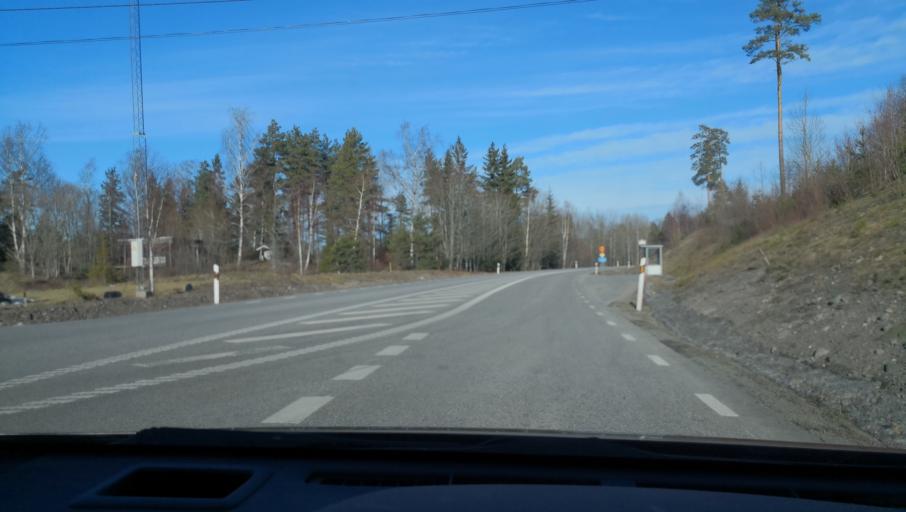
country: SE
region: Uppsala
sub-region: Uppsala Kommun
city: Vattholma
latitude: 60.0733
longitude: 17.7586
